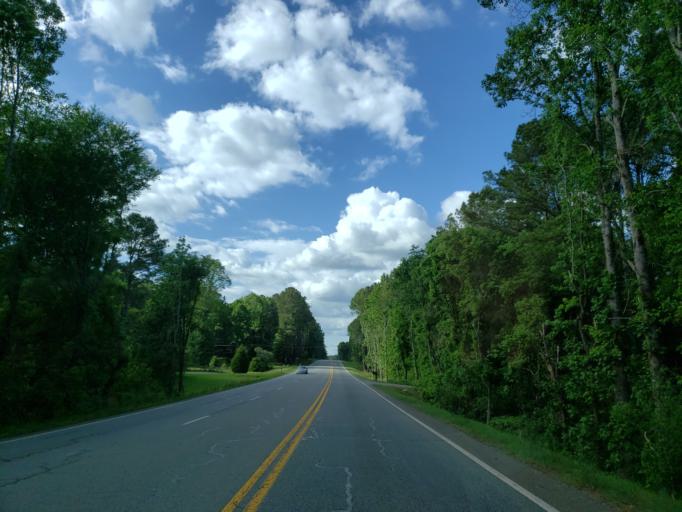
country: US
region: Georgia
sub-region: Bartow County
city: Cartersville
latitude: 34.2520
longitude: -84.8578
